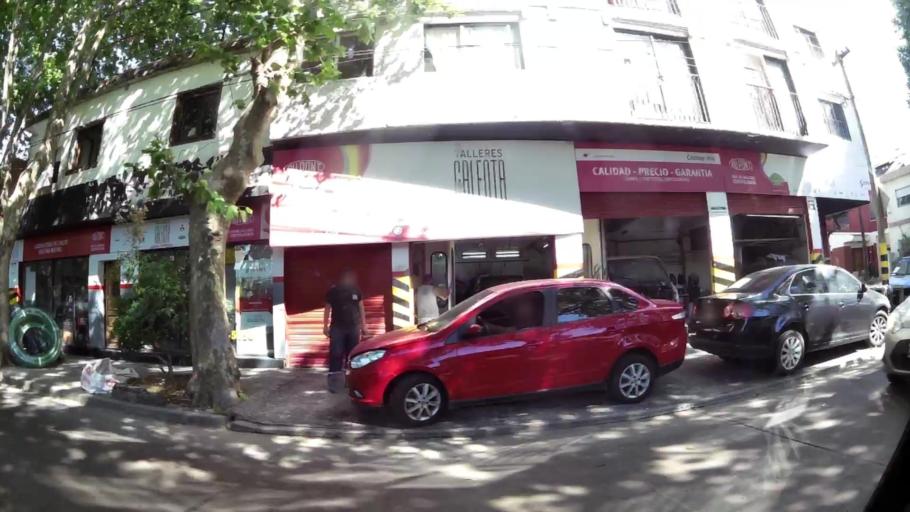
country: AR
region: Buenos Aires
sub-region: Partido de San Isidro
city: San Isidro
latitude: -34.4674
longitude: -58.5267
